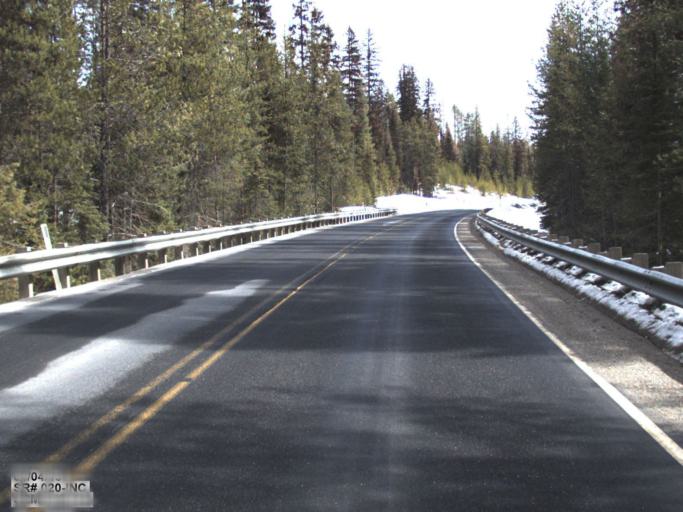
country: US
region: Washington
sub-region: Stevens County
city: Colville
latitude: 48.6387
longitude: -117.5300
